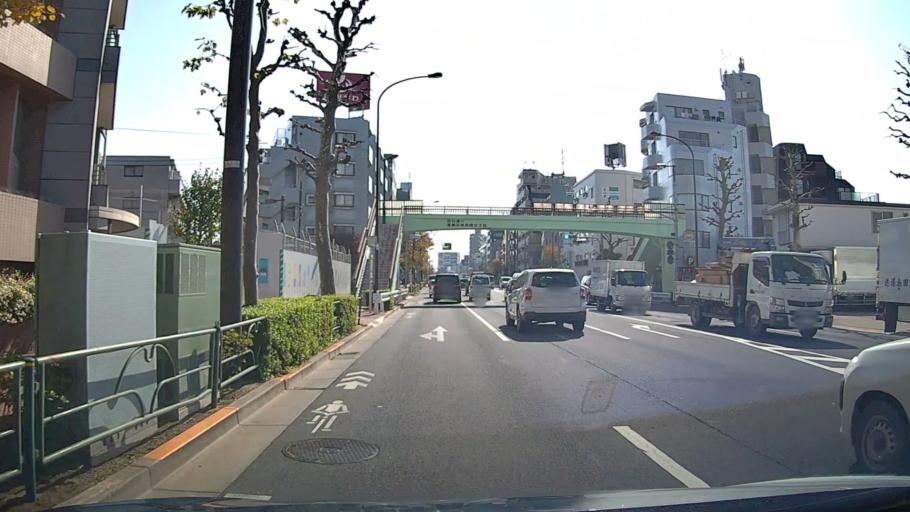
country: JP
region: Tokyo
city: Tokyo
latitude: 35.7271
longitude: 139.6816
